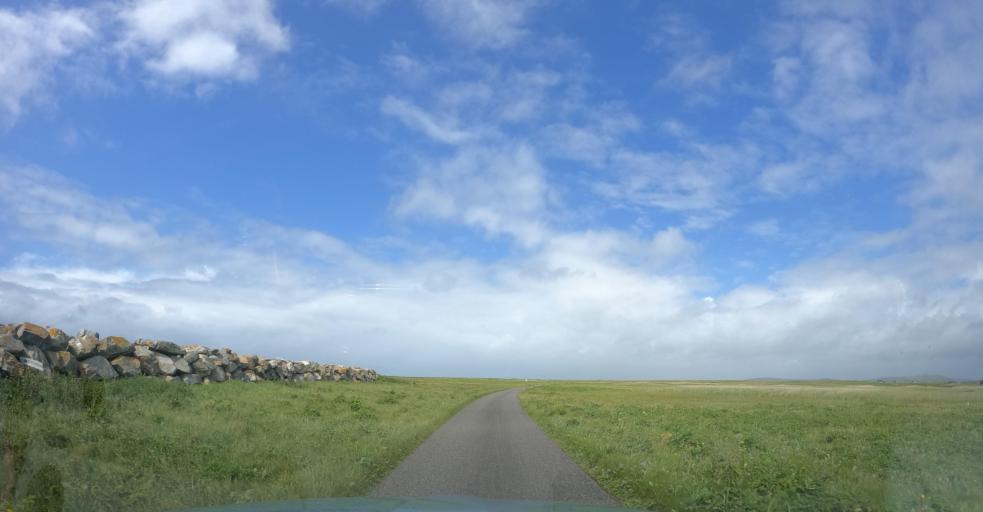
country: GB
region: Scotland
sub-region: Eilean Siar
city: Isle of South Uist
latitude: 57.2827
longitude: -7.4196
